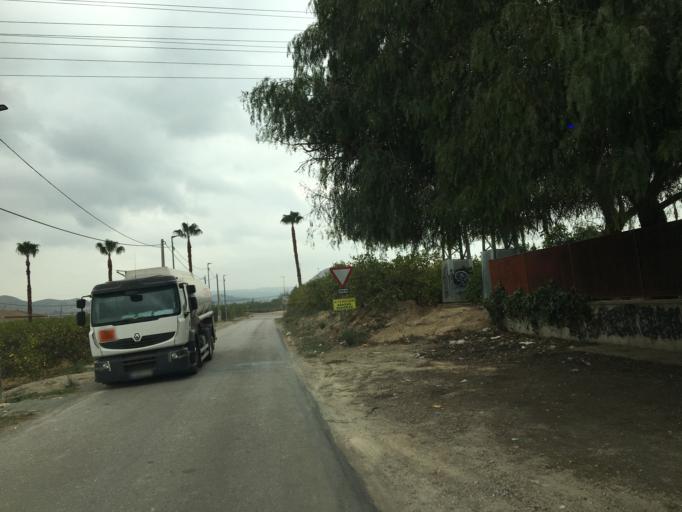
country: ES
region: Murcia
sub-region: Murcia
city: Santomera
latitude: 38.0811
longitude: -1.0556
